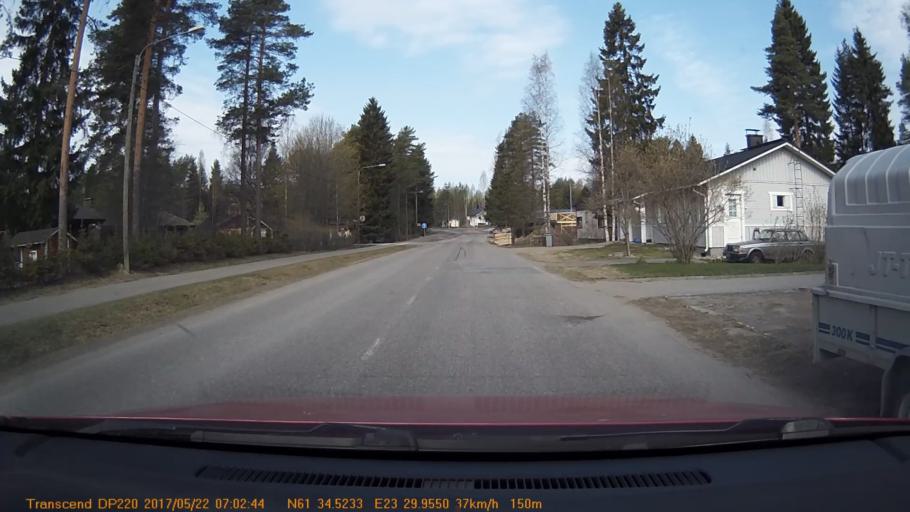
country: FI
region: Pirkanmaa
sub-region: Tampere
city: Yloejaervi
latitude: 61.5753
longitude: 23.4995
